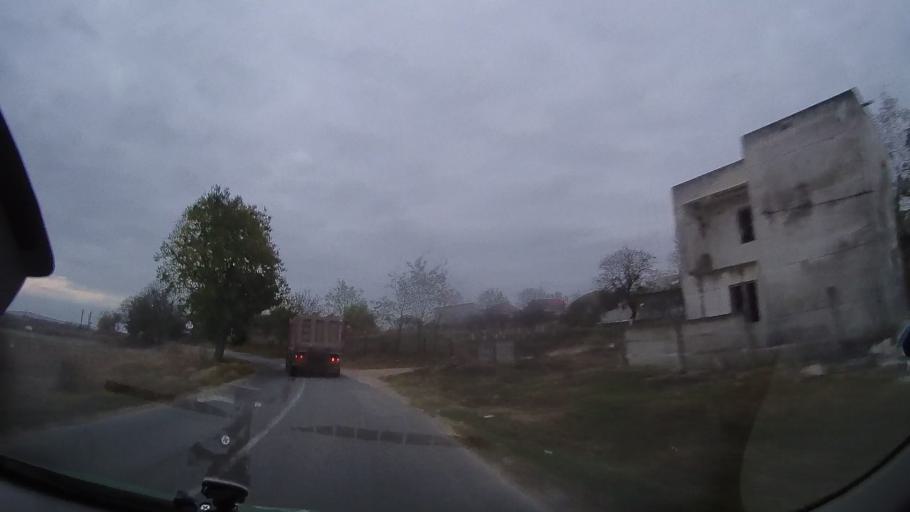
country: RO
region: Tulcea
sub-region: Comuna Mihai Bravu
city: Mihai Bravu
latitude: 44.9544
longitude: 28.6537
